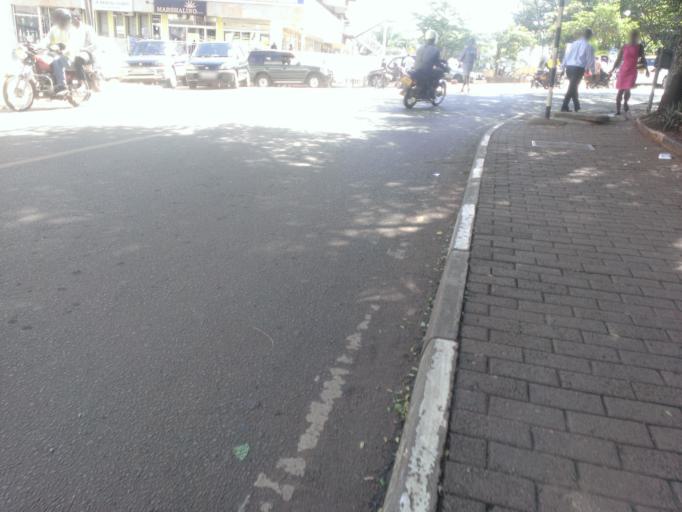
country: UG
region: Central Region
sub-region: Kampala District
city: Kampala
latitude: 0.3149
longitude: 32.5826
